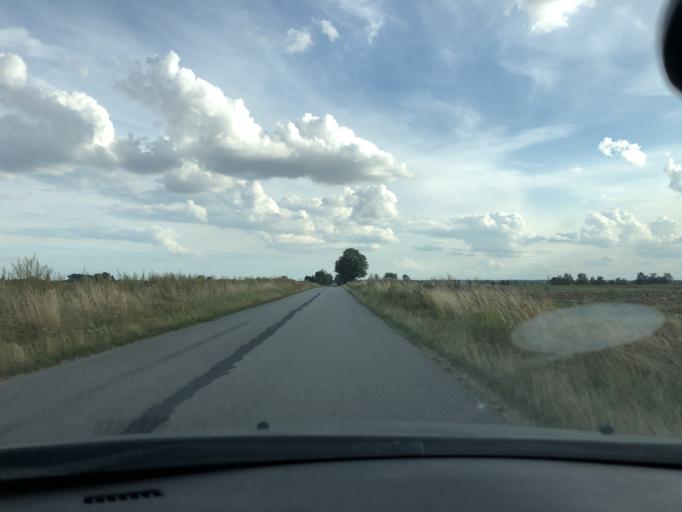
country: PL
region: Lodz Voivodeship
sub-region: Powiat wieruszowski
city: Walichnowy
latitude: 51.2546
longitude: 18.3904
